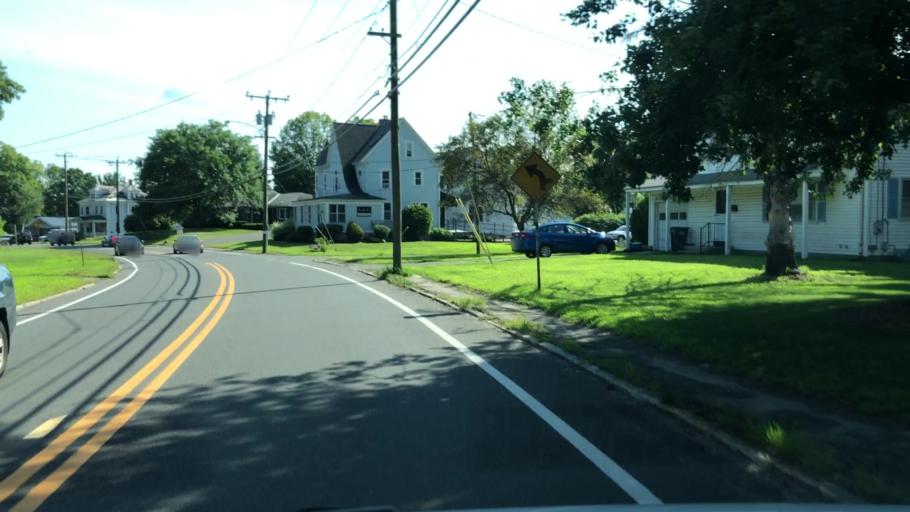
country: US
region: Massachusetts
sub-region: Hampshire County
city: Easthampton
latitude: 42.2765
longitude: -72.6740
